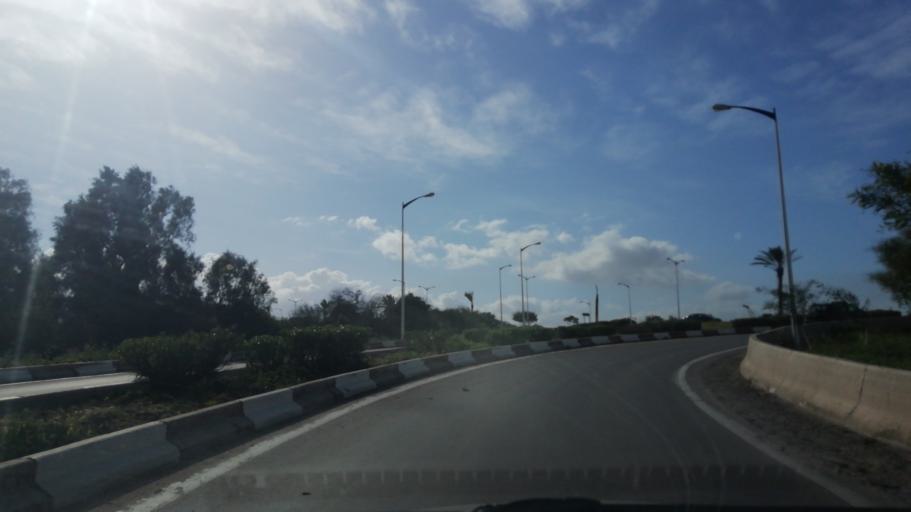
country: DZ
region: Mostaganem
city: Mostaganem
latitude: 35.9138
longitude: 0.0736
